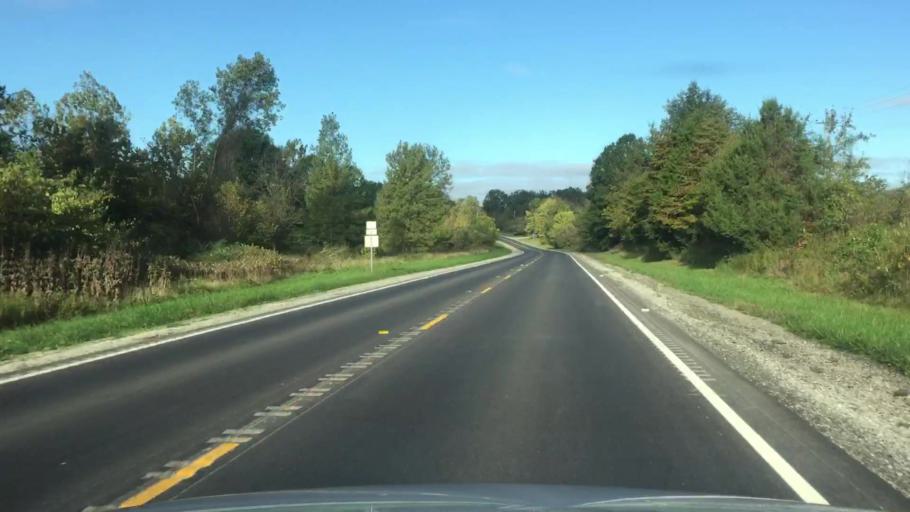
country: US
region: Missouri
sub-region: Howard County
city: New Franklin
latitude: 38.9957
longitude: -92.5731
